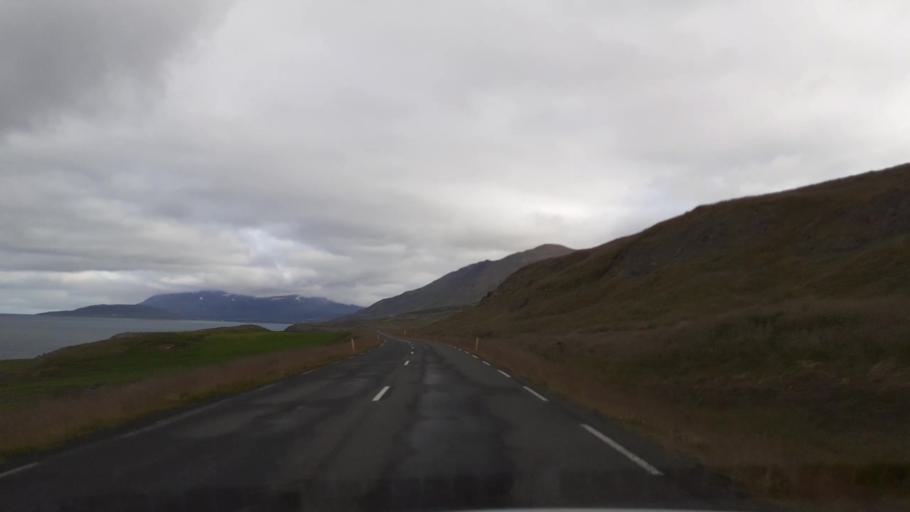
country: IS
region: Northeast
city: Akureyri
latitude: 65.8025
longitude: -18.0561
